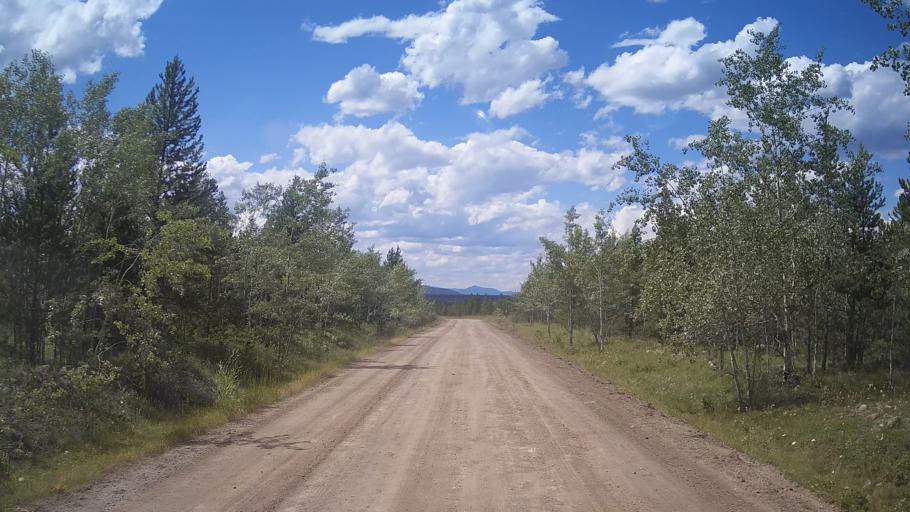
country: CA
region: British Columbia
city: Lillooet
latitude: 51.3413
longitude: -121.9258
